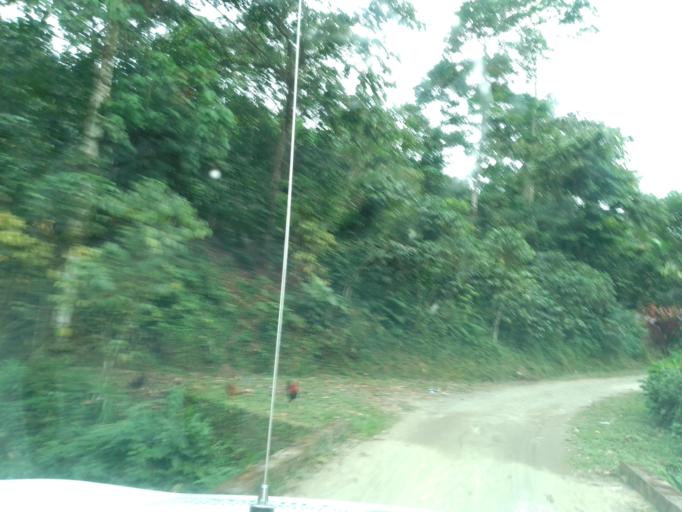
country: MX
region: Chiapas
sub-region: Union Juarez
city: Santo Domingo
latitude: 15.0568
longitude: -92.1105
